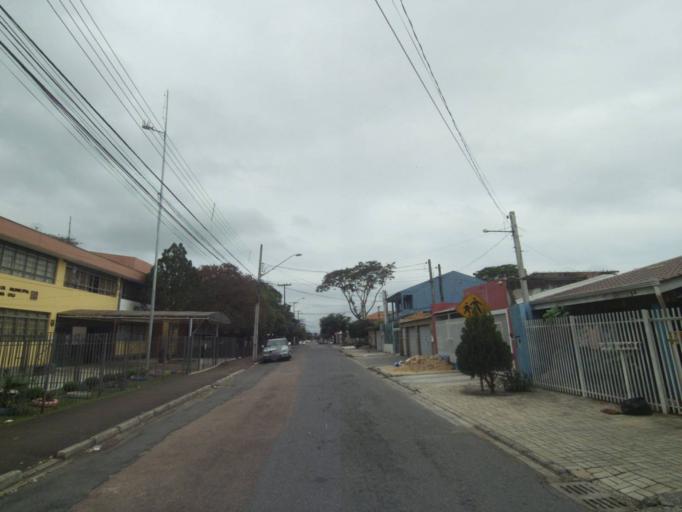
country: BR
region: Parana
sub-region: Sao Jose Dos Pinhais
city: Sao Jose dos Pinhais
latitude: -25.5400
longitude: -49.2517
